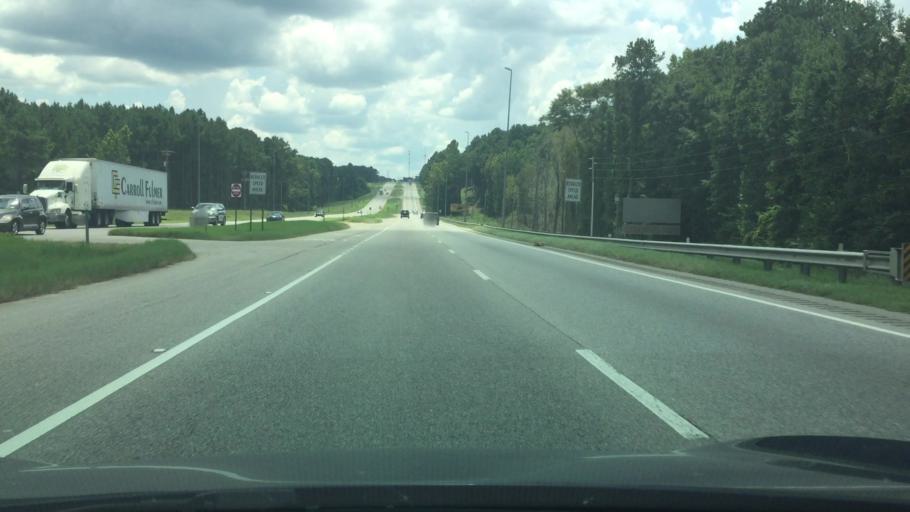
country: US
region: Alabama
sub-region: Pike County
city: Troy
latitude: 31.8220
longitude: -85.9947
